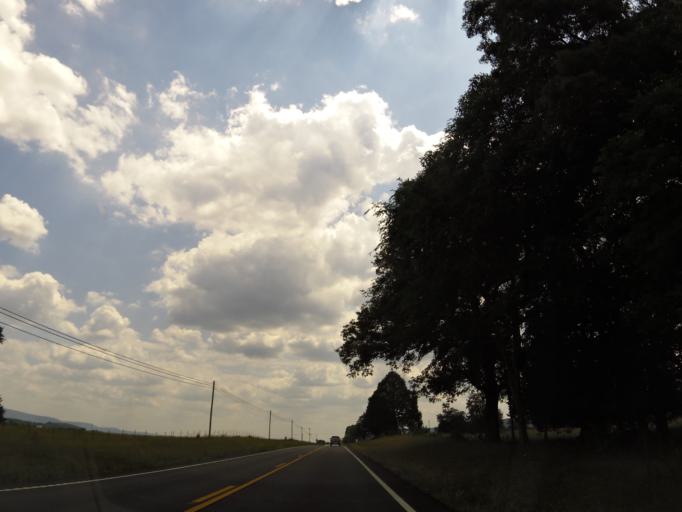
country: US
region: Tennessee
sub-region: Sequatchie County
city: Dunlap
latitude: 35.4567
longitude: -85.3311
